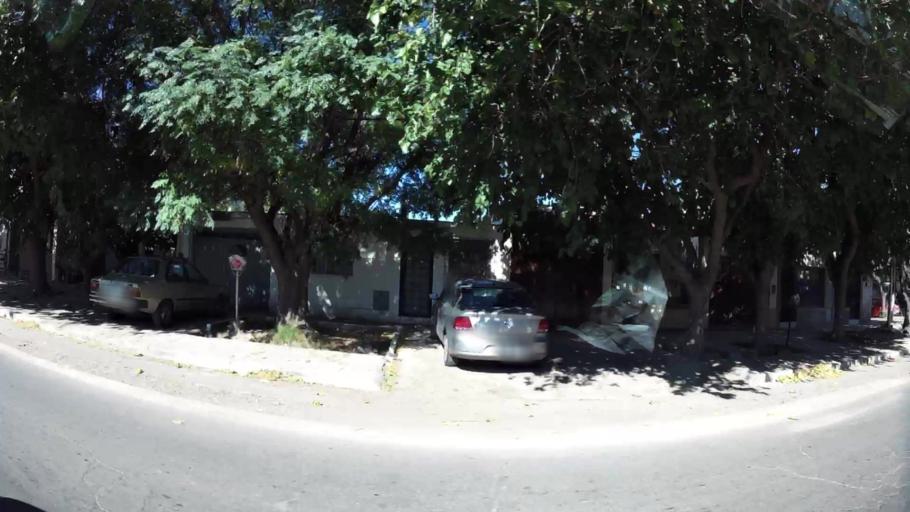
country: AR
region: Mendoza
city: Las Heras
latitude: -32.8482
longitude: -68.8206
